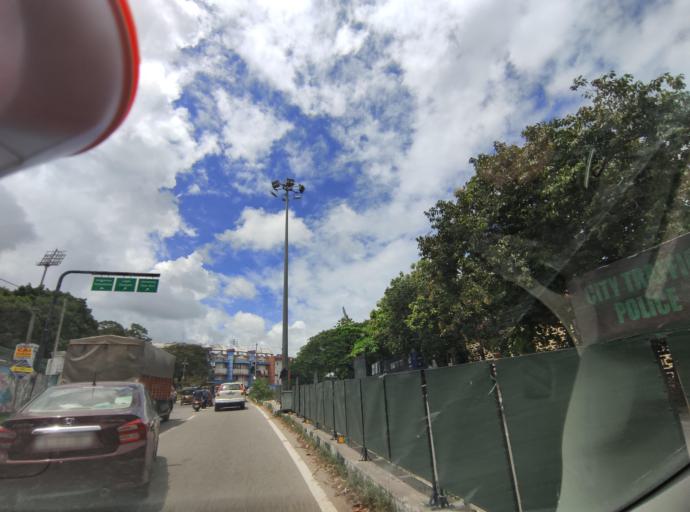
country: IN
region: Kerala
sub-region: Thiruvananthapuram
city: Thiruvananthapuram
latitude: 8.5087
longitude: 76.9497
